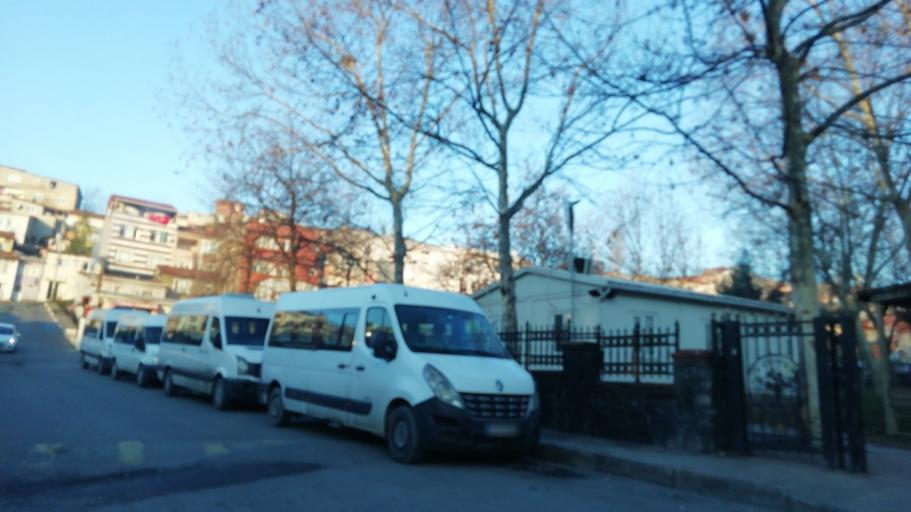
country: TR
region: Istanbul
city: Sisli
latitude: 41.0419
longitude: 28.9723
